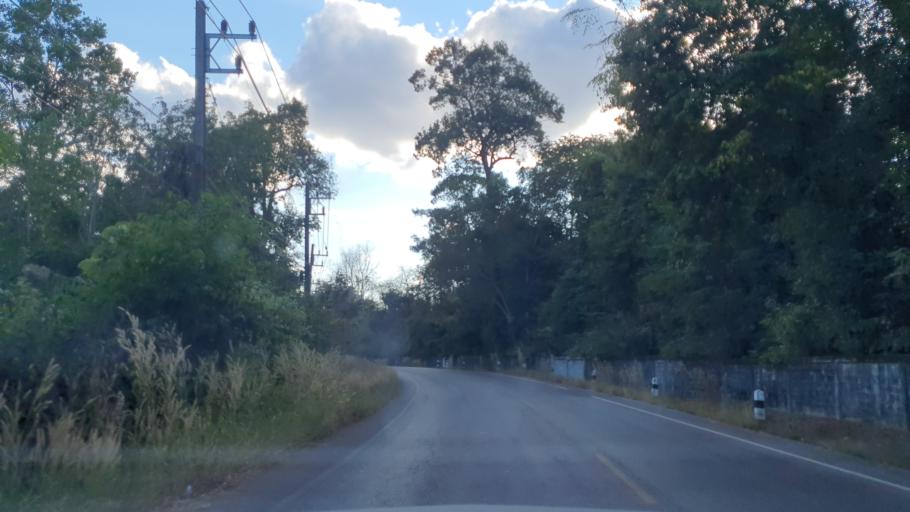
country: TH
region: Changwat Bueng Kan
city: Si Wilai
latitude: 18.1333
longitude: 103.8852
